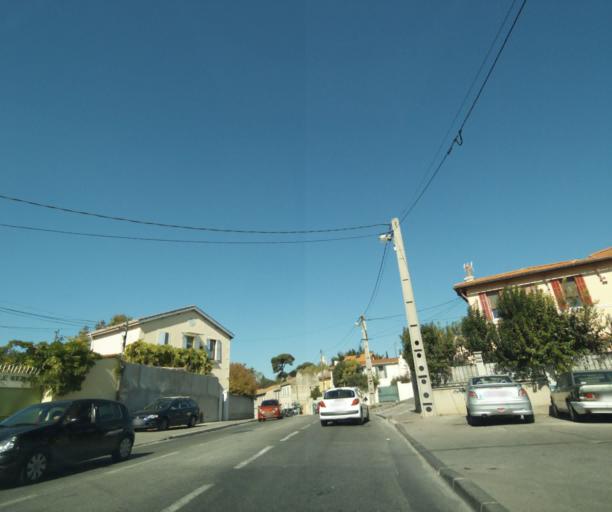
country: FR
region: Provence-Alpes-Cote d'Azur
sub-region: Departement des Bouches-du-Rhone
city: Marseille 14
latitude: 43.3364
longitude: 5.3973
